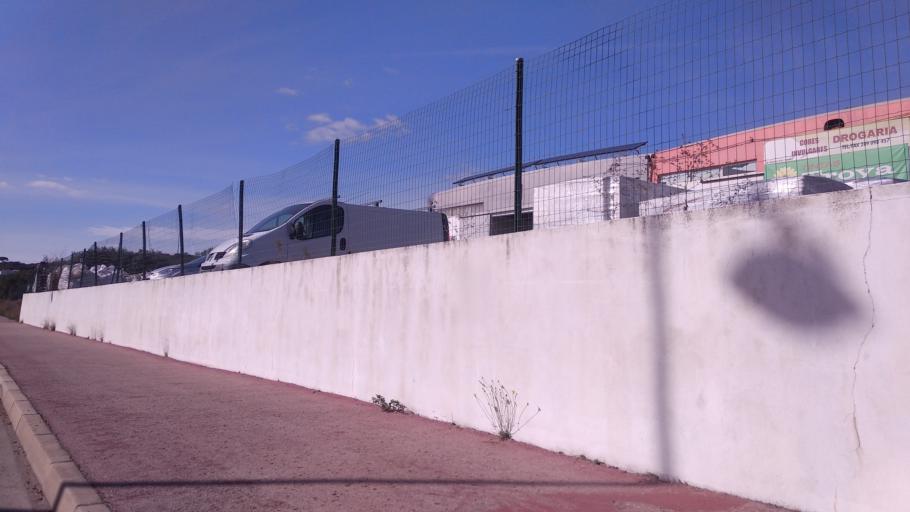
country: PT
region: Faro
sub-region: Sao Bras de Alportel
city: Sao Bras de Alportel
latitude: 37.1593
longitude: -7.8906
